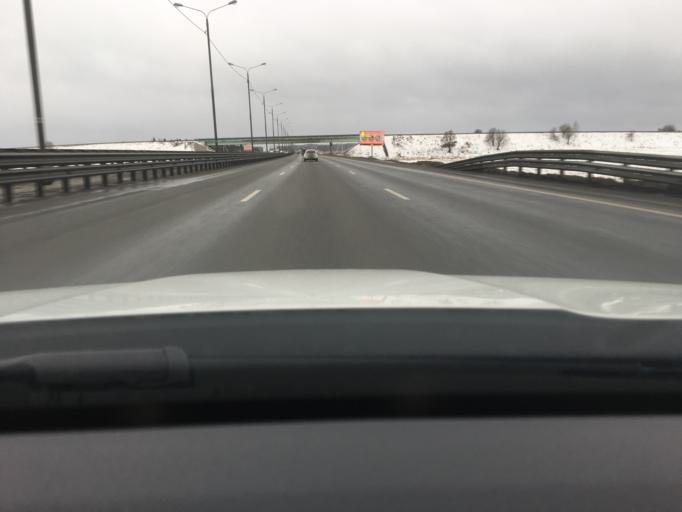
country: RU
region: Moskovskaya
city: Novyy Byt
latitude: 55.0610
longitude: 37.5642
